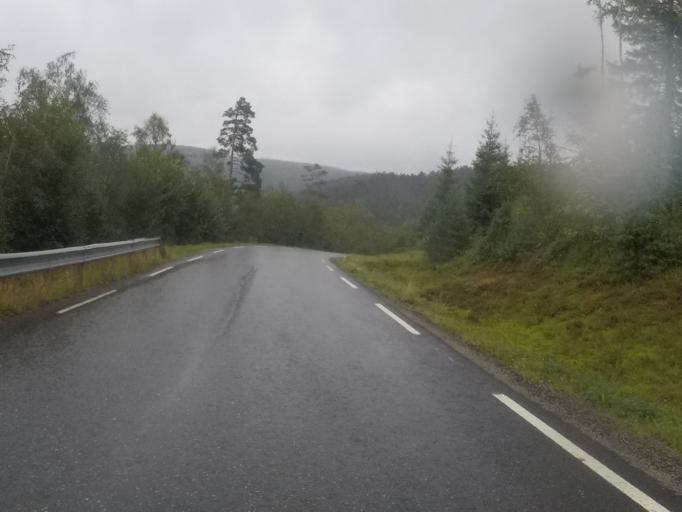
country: NO
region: Vest-Agder
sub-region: Lyngdal
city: Lyngdal
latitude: 58.2389
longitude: 7.1471
